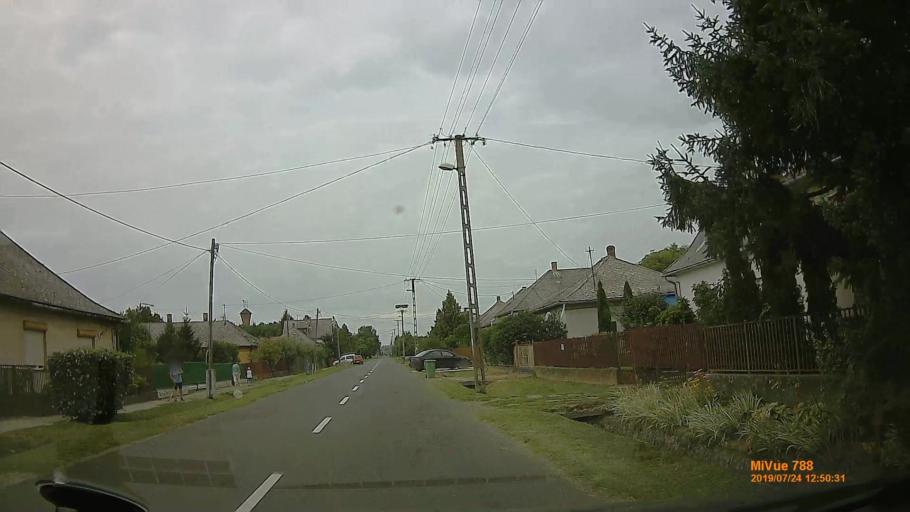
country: HU
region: Szabolcs-Szatmar-Bereg
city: Aranyosapati
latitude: 48.1886
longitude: 22.3104
